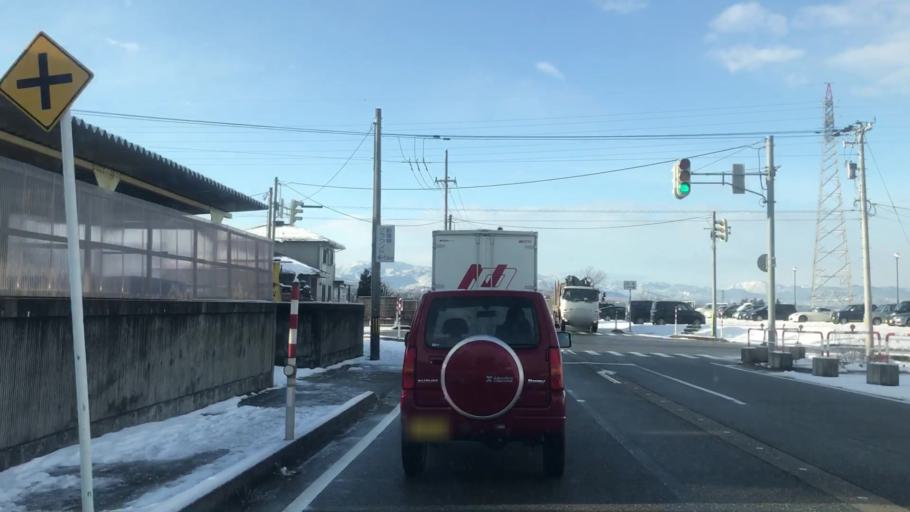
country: JP
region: Toyama
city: Kamiichi
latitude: 36.6227
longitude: 137.2914
